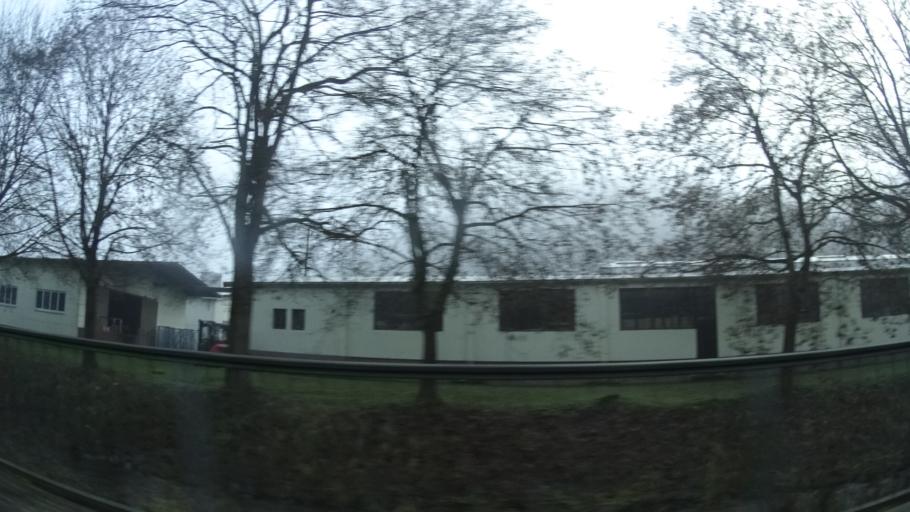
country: DE
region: Bavaria
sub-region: Regierungsbezirk Unterfranken
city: Neunkirchen
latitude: 49.6695
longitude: 9.3745
